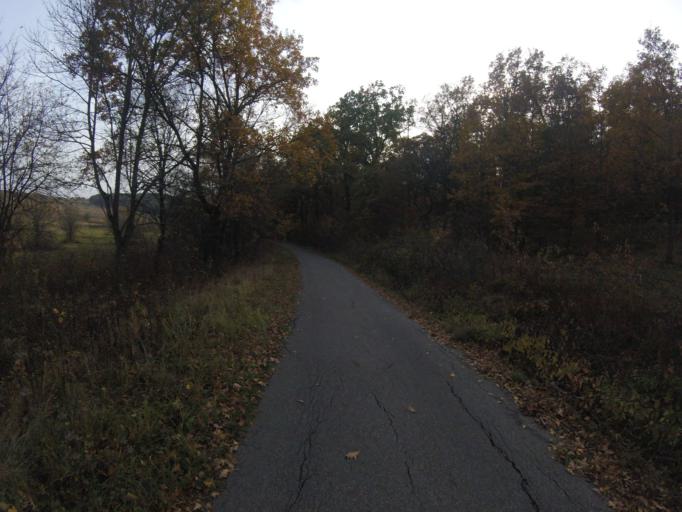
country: HU
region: Borsod-Abauj-Zemplen
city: Gonc
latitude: 48.5197
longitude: 21.4565
